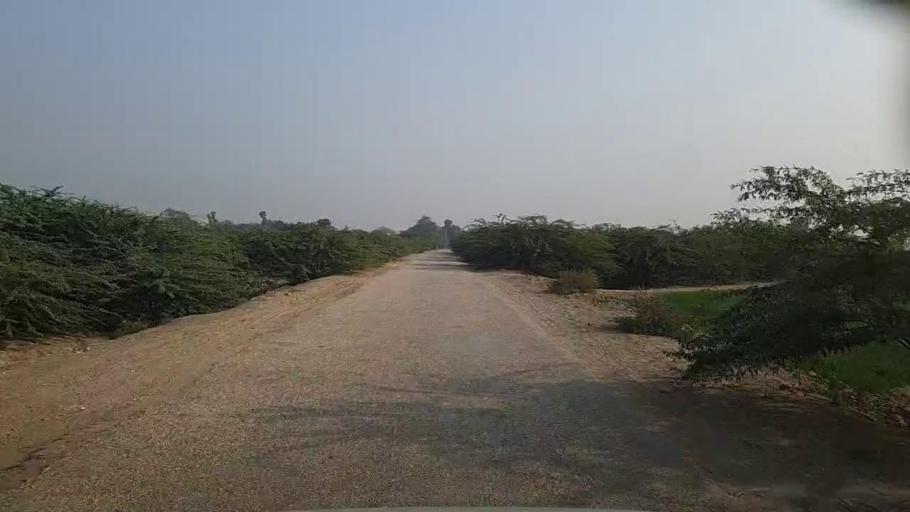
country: PK
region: Sindh
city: Kandiari
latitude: 27.0437
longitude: 68.4746
